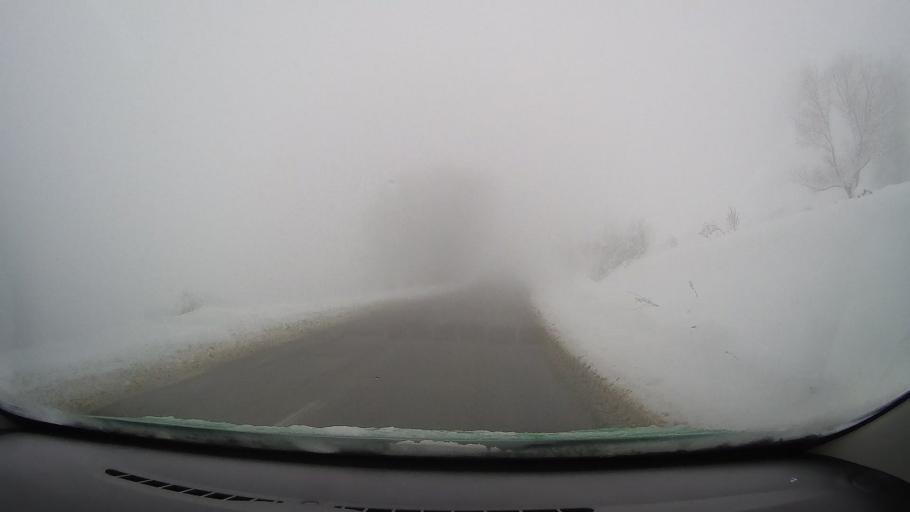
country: RO
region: Sibiu
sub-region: Comuna Poiana Sibiului
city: Poiana Sibiului
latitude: 45.8096
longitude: 23.7450
